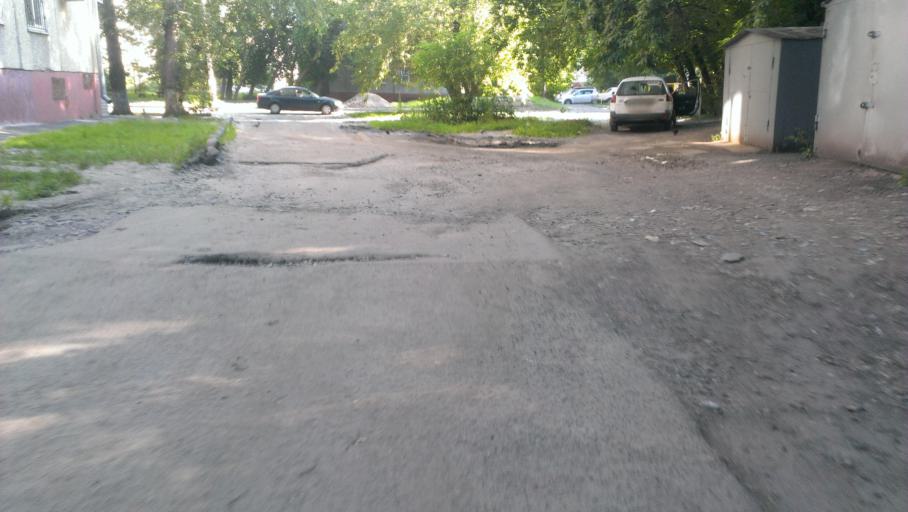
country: RU
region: Altai Krai
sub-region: Gorod Barnaulskiy
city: Barnaul
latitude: 53.3656
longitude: 83.6954
